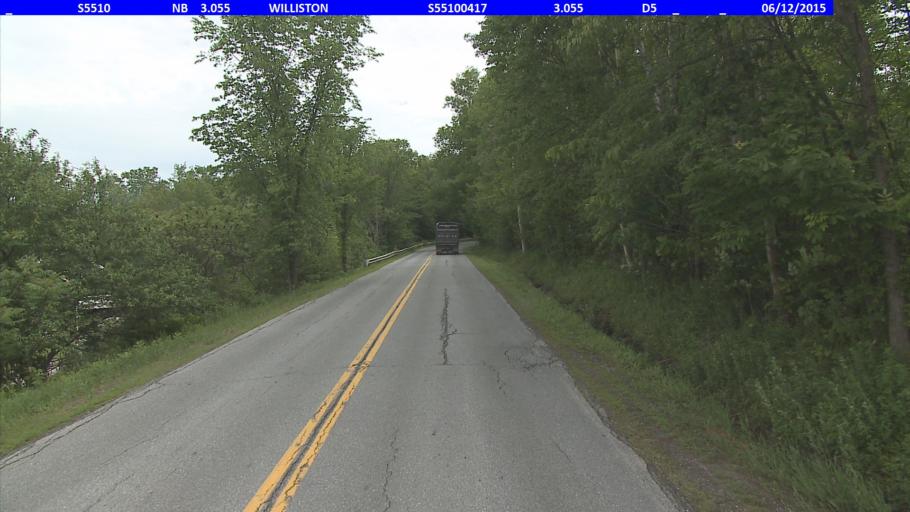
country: US
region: Vermont
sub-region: Chittenden County
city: Williston
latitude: 44.4155
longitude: -73.0866
